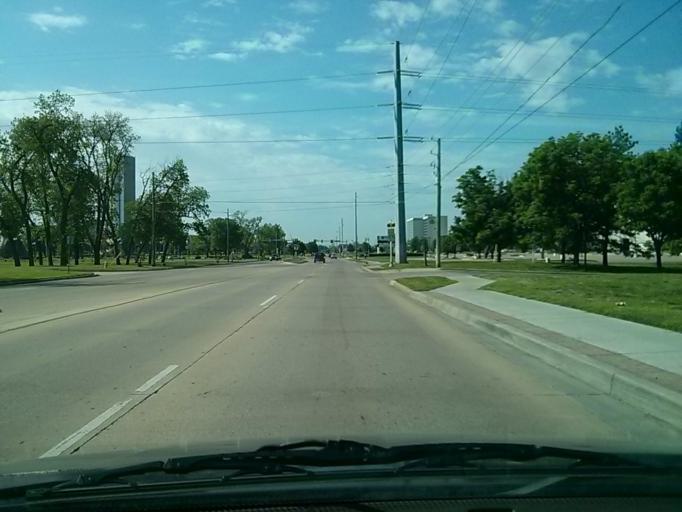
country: US
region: Oklahoma
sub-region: Tulsa County
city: Jenks
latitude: 36.0542
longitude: -95.9579
